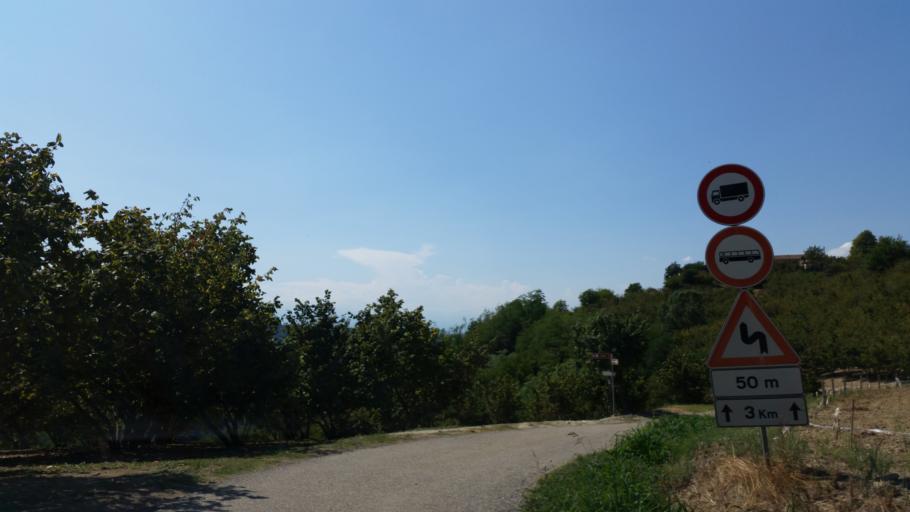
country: IT
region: Piedmont
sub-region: Provincia di Cuneo
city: Sinio
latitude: 44.6056
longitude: 8.0299
